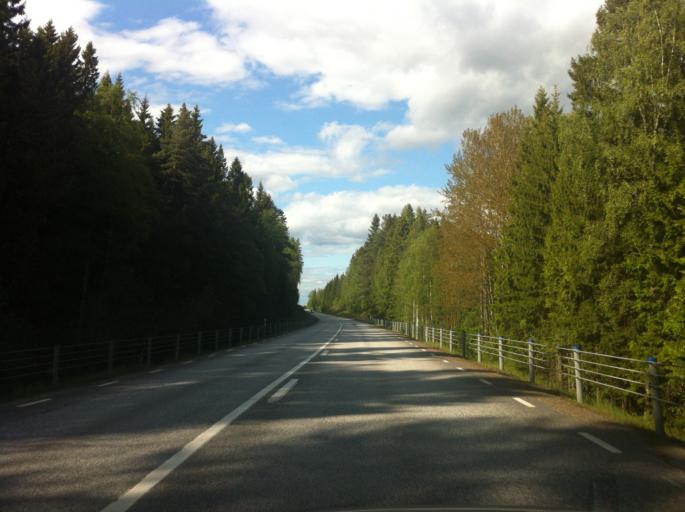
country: SE
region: Vaermland
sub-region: Storfors Kommun
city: Storfors
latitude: 59.4648
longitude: 14.2550
